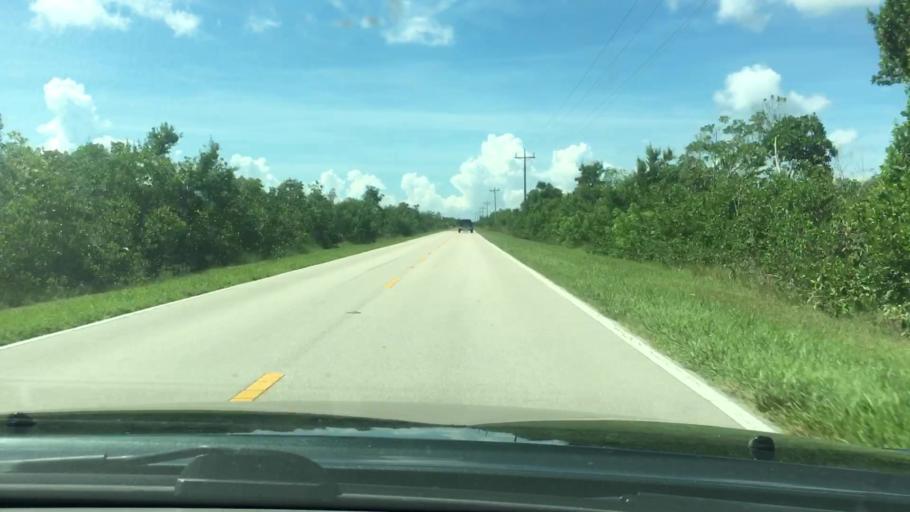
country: US
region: Florida
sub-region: Collier County
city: Marco
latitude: 25.9462
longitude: -81.6435
